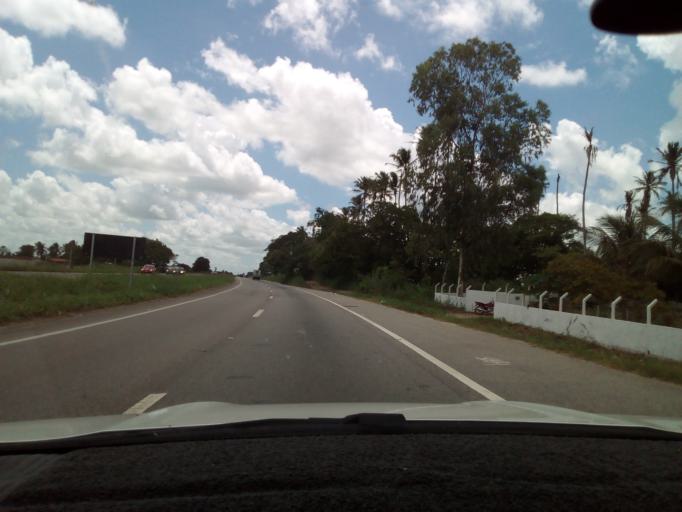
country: BR
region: Paraiba
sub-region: Pilar
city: Pilar
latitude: -7.1919
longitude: -35.2226
